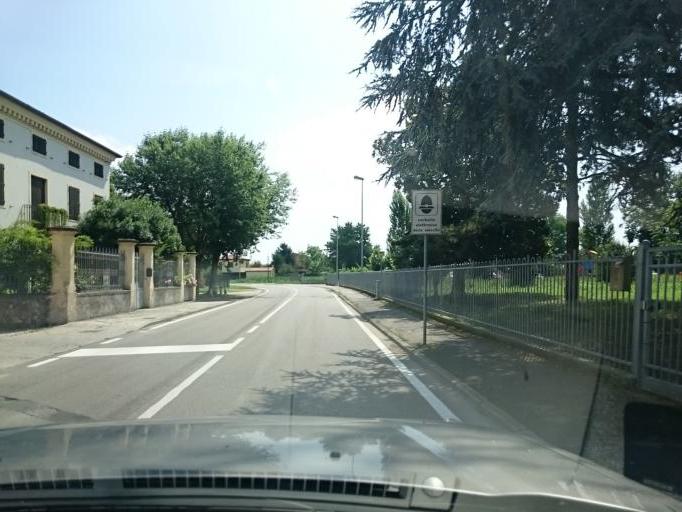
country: IT
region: Veneto
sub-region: Provincia di Padova
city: Albignasego
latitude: 45.3387
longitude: 11.8838
